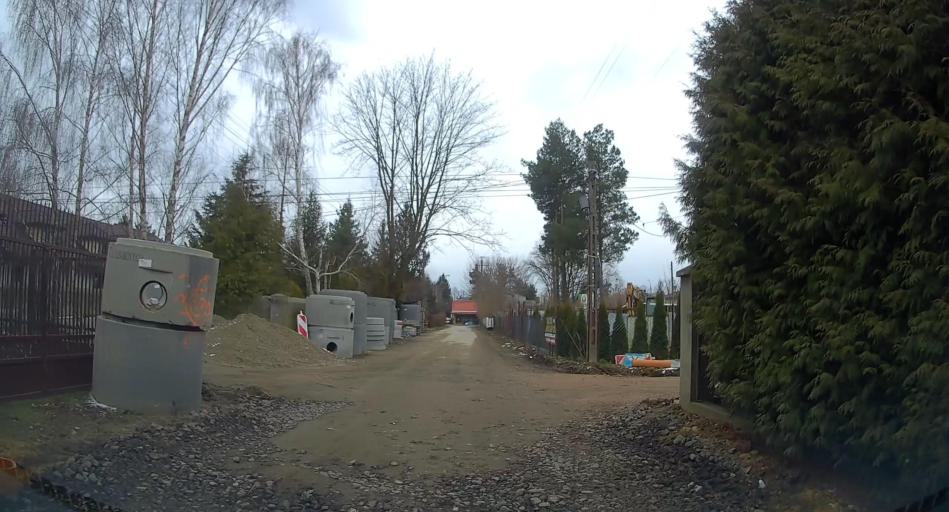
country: PL
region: Masovian Voivodeship
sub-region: Powiat piaseczynski
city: Piaseczno
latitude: 52.0534
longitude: 20.9991
